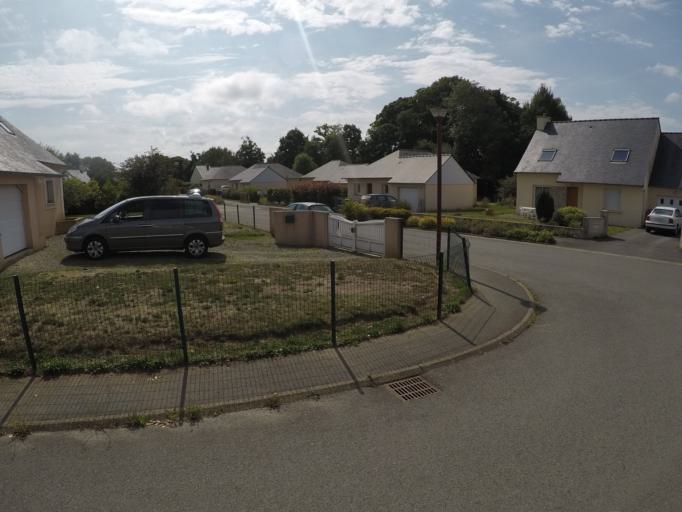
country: FR
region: Brittany
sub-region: Departement des Cotes-d'Armor
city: Goudelin
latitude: 48.6014
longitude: -3.0215
